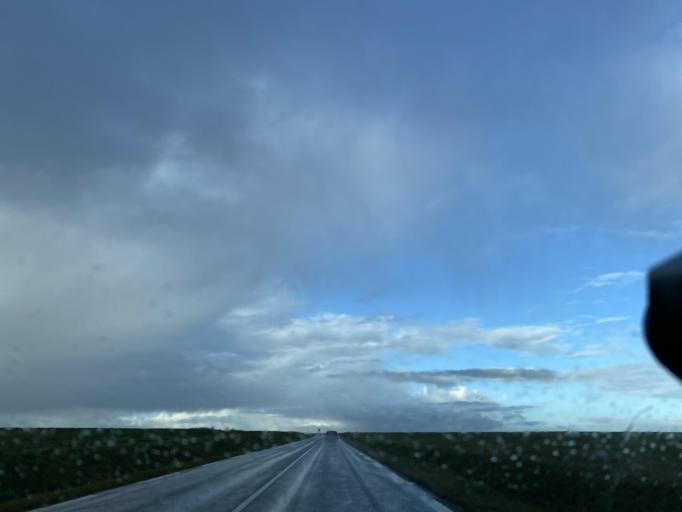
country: FR
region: Centre
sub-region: Departement d'Eure-et-Loir
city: Chateauneuf-en-Thymerais
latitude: 48.5573
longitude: 1.2777
